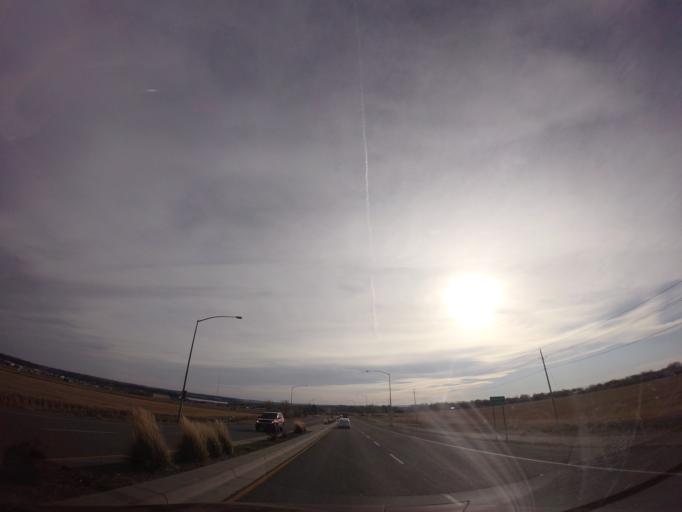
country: US
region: Montana
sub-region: Yellowstone County
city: Billings
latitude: 45.7382
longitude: -108.6175
